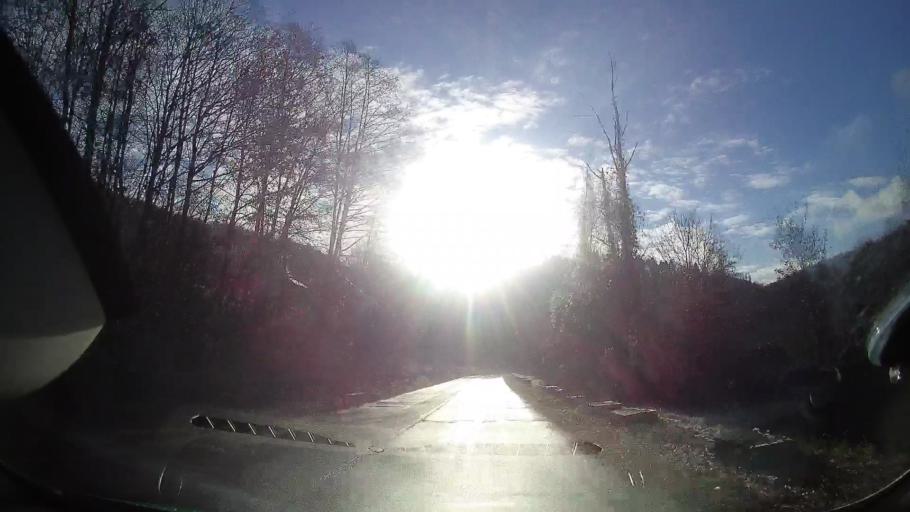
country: RO
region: Alba
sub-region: Comuna Sohodol
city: Sohodol
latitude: 46.3674
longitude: 23.0288
